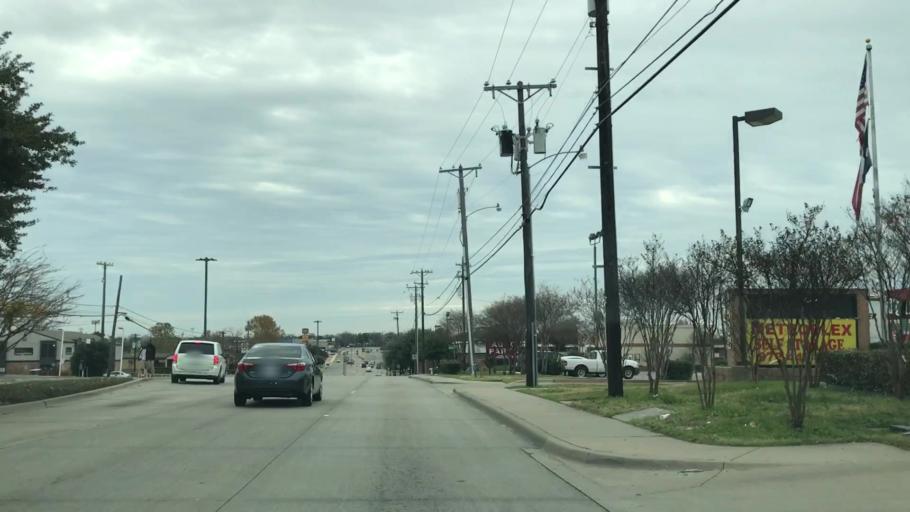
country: US
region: Texas
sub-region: Dallas County
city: Carrollton
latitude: 32.9422
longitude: -96.8906
